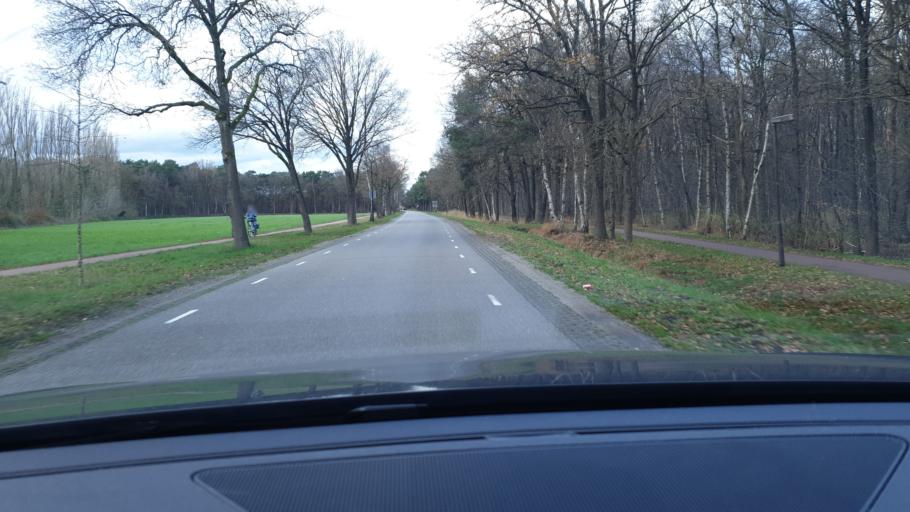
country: NL
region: North Brabant
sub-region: Gemeente Waalre
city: Waalre
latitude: 51.3828
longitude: 5.4167
